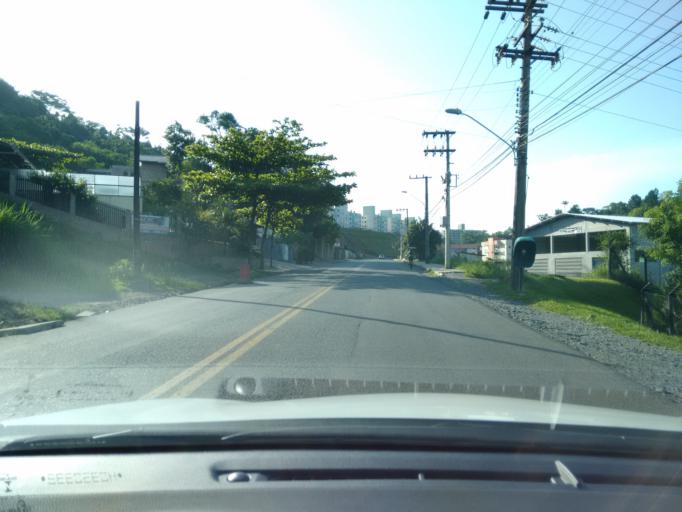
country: BR
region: Santa Catarina
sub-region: Blumenau
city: Blumenau
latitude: -26.8597
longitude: -49.1033
